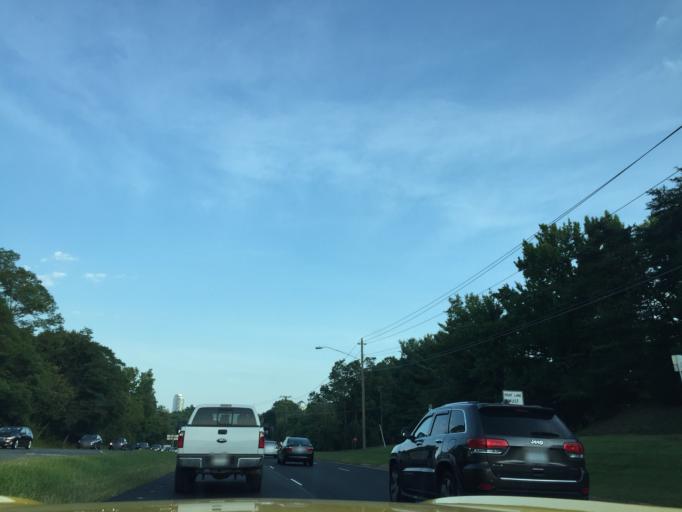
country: US
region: Virginia
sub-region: Fairfax County
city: Wolf Trap
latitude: 38.9421
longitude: -77.2545
